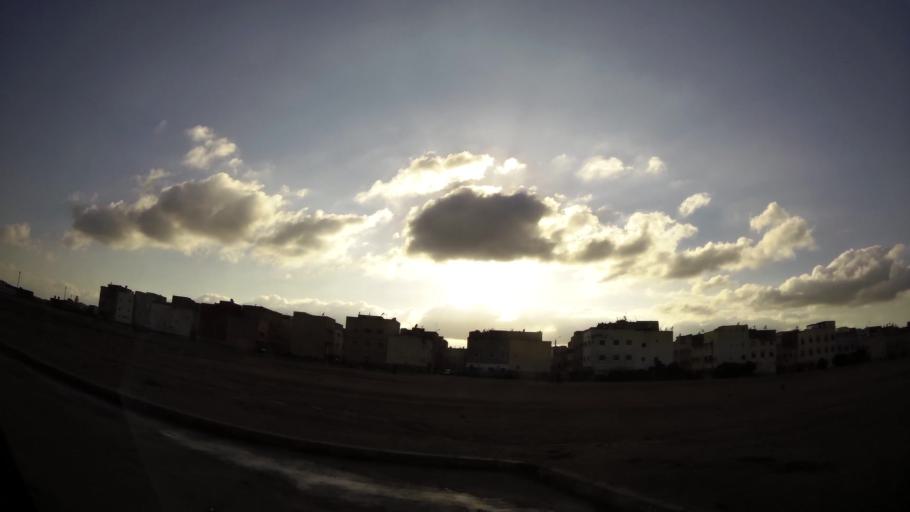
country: MA
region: Chaouia-Ouardigha
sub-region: Settat Province
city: Settat
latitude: 33.0008
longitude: -7.6363
